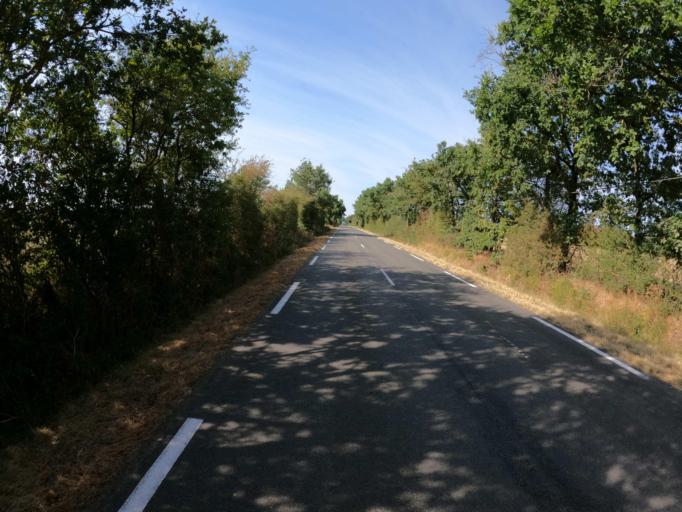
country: FR
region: Pays de la Loire
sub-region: Departement de la Vendee
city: Falleron
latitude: 46.8624
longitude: -1.7107
